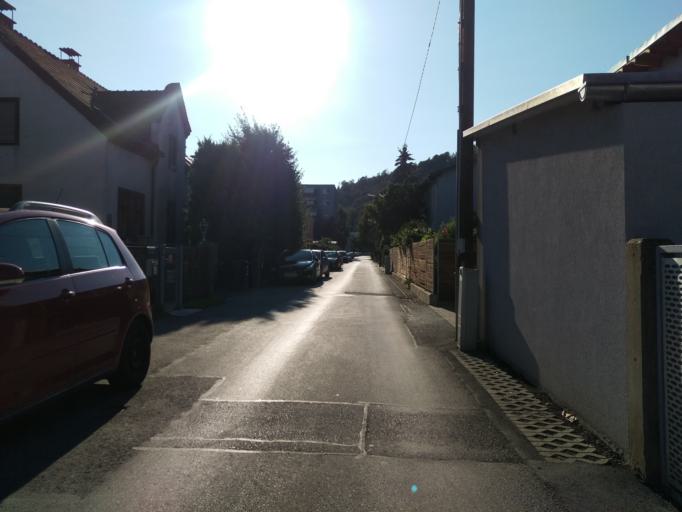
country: AT
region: Styria
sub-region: Politischer Bezirk Graz-Umgebung
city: Seiersberg
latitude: 47.0181
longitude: 15.4042
